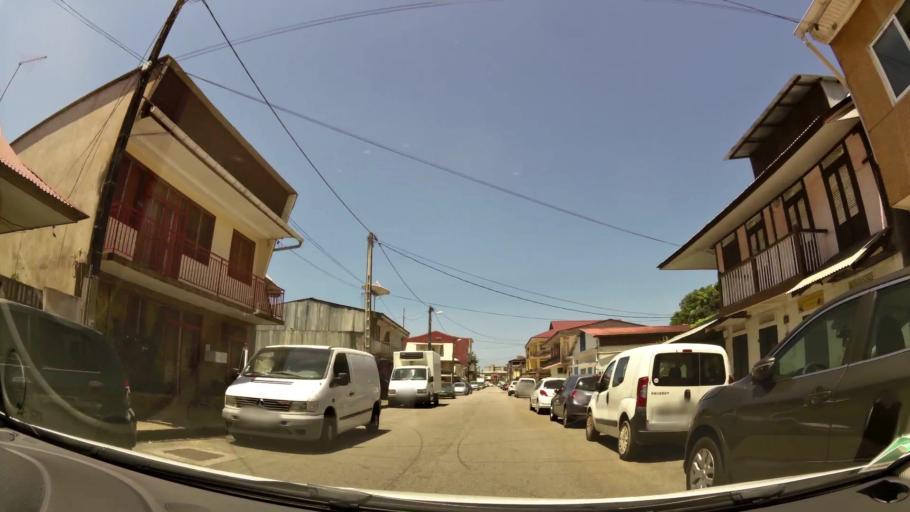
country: GF
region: Guyane
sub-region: Guyane
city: Cayenne
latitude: 4.9345
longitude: -52.3313
